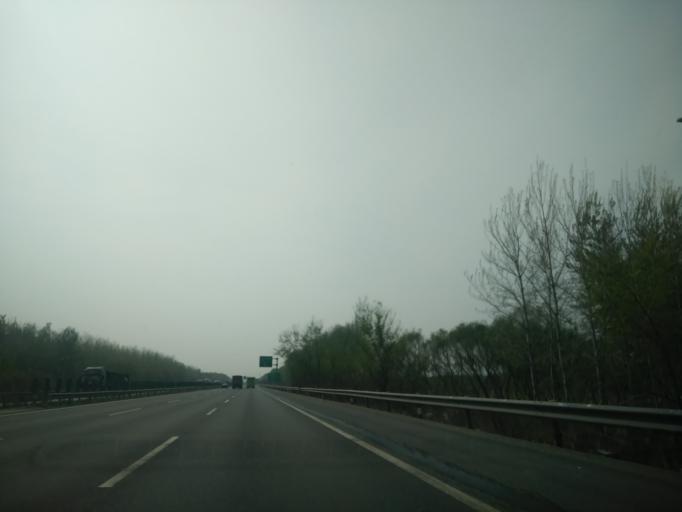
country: CN
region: Beijing
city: Xiji
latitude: 39.7991
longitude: 116.9268
